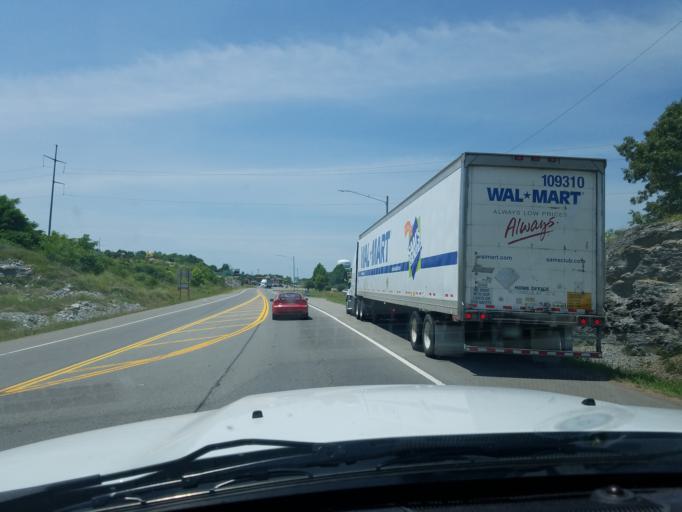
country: US
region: Tennessee
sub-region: Sumner County
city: Westmoreland
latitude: 36.5545
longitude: -86.2376
